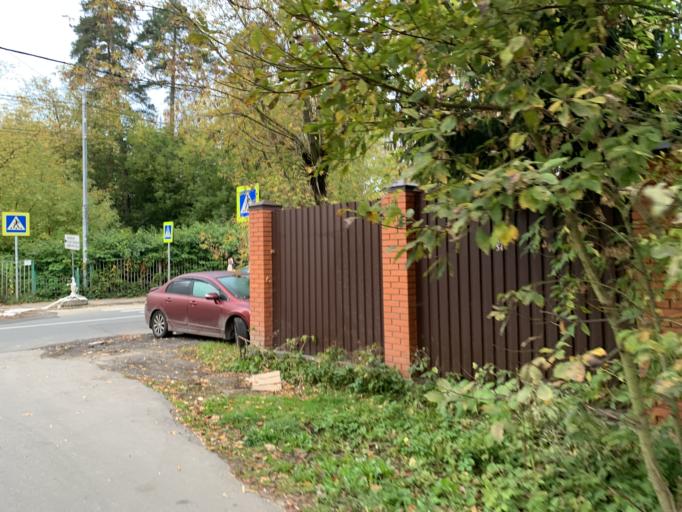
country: RU
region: Moskovskaya
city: Korolev
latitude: 55.9305
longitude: 37.7877
